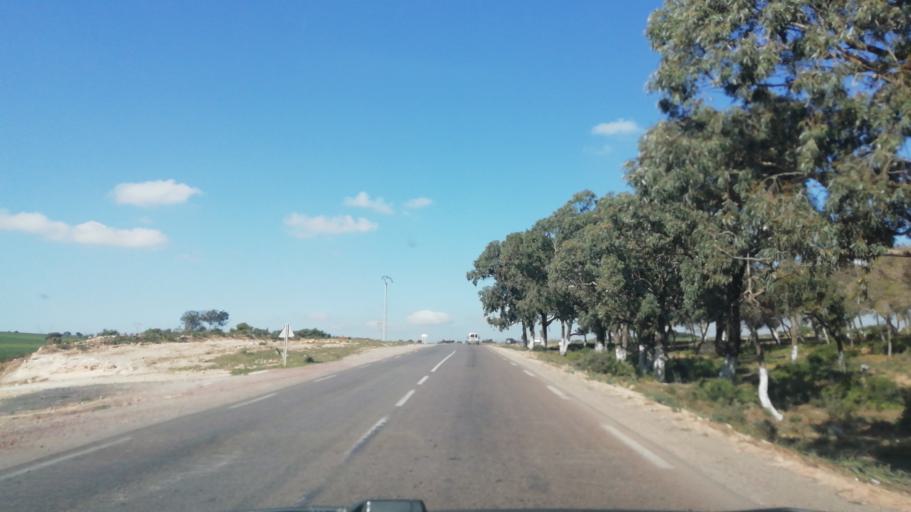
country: DZ
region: Oran
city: Ain el Bya
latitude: 35.7142
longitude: -0.2301
